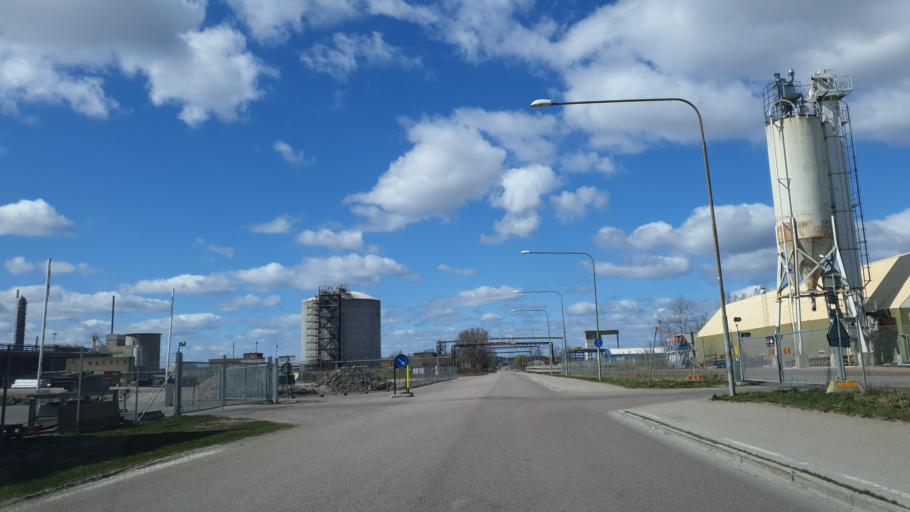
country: SE
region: Vaestmanland
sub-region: Kopings Kommun
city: Koping
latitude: 59.4991
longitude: 16.0181
